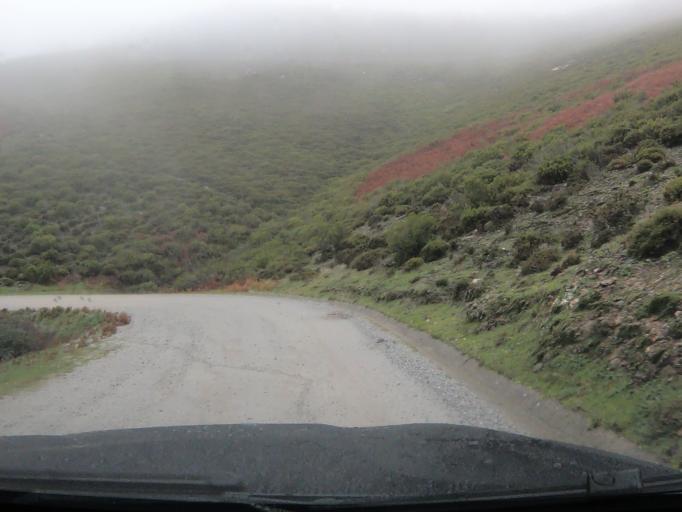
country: PT
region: Vila Real
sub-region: Mondim de Basto
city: Mondim de Basto
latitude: 41.3226
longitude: -7.8699
